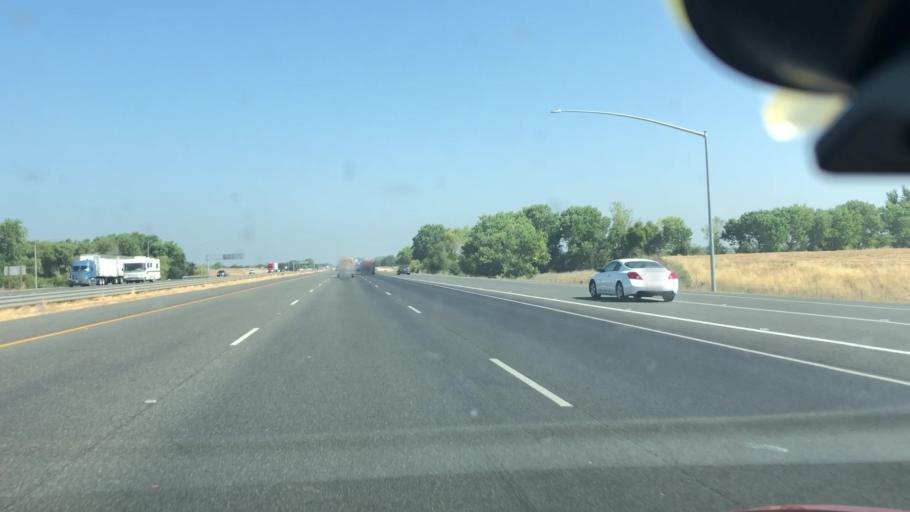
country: US
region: California
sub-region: Sacramento County
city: Laguna
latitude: 38.4291
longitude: -121.4878
